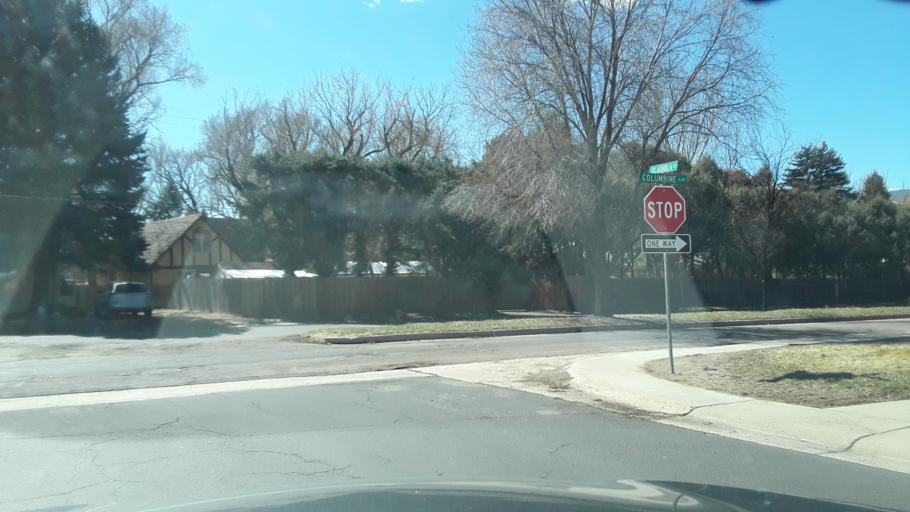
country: US
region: Colorado
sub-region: El Paso County
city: Colorado Springs
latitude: 38.8753
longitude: -104.7991
